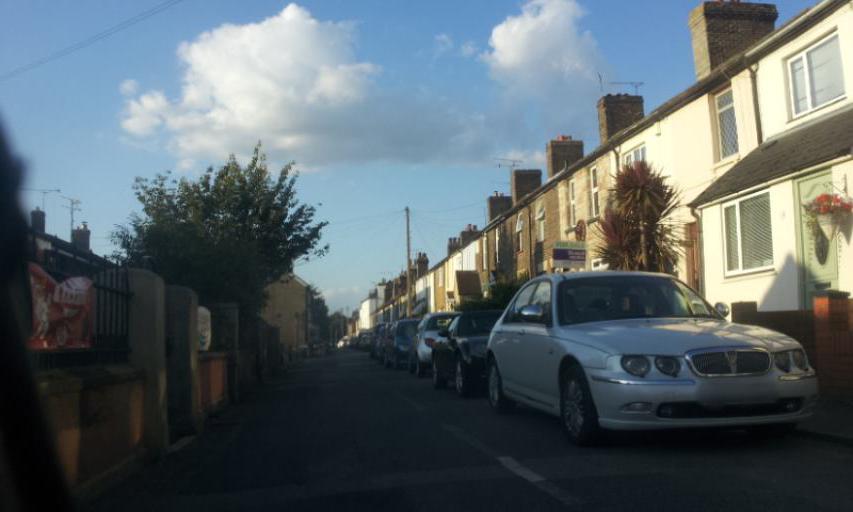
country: GB
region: England
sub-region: Medway
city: Halling
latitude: 51.3474
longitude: 0.4580
